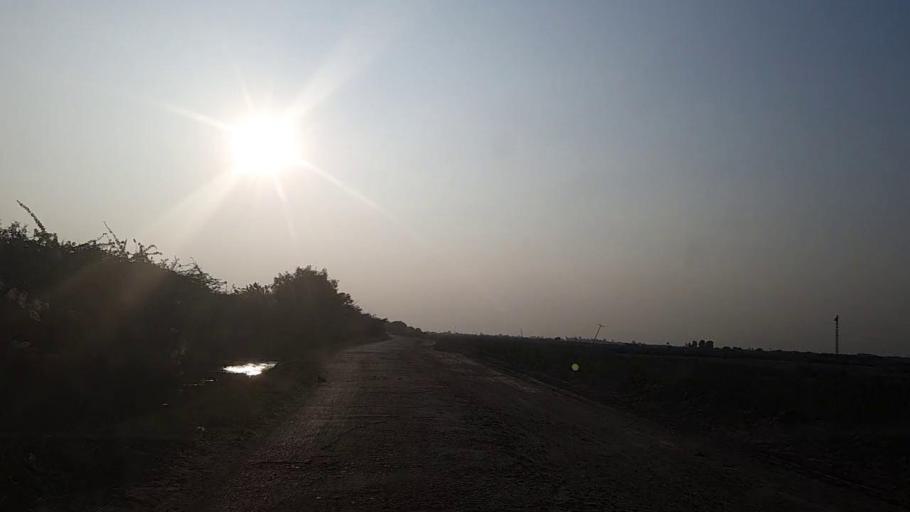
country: PK
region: Sindh
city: Mirpur Sakro
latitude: 24.5617
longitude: 67.6110
